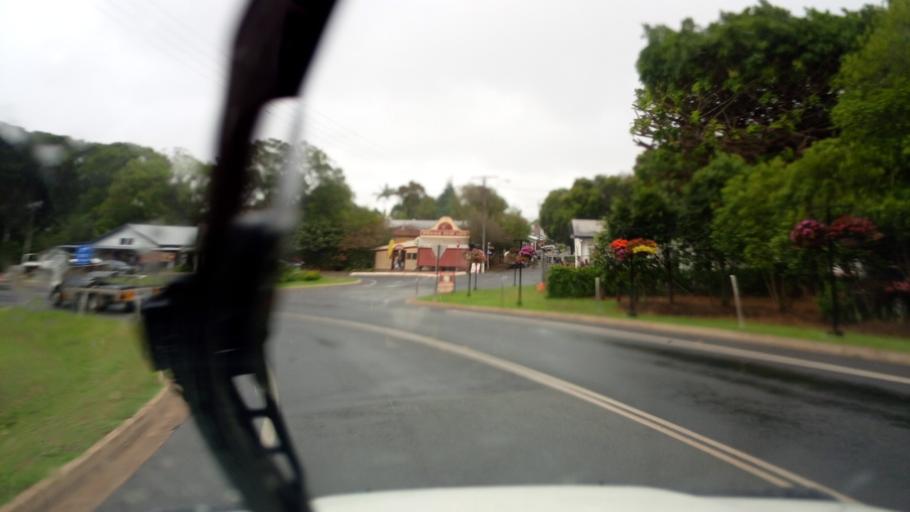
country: AU
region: Queensland
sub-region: Tablelands
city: Tolga
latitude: -17.2711
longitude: 145.5837
